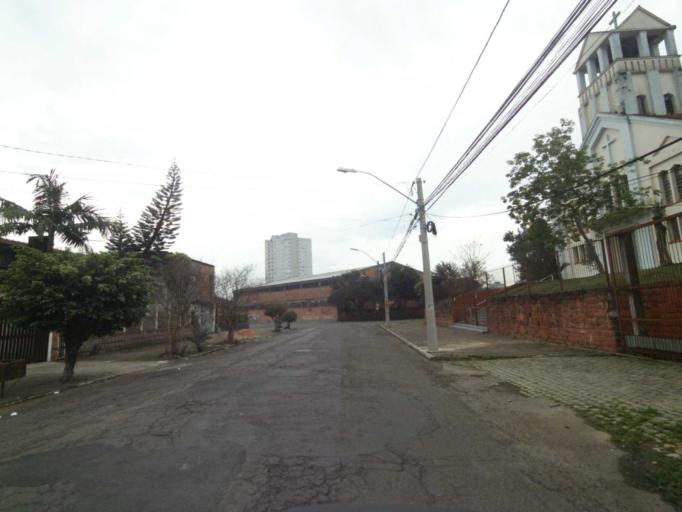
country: BR
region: Rio Grande do Sul
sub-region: Sao Leopoldo
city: Sao Leopoldo
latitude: -29.7730
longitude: -51.1516
